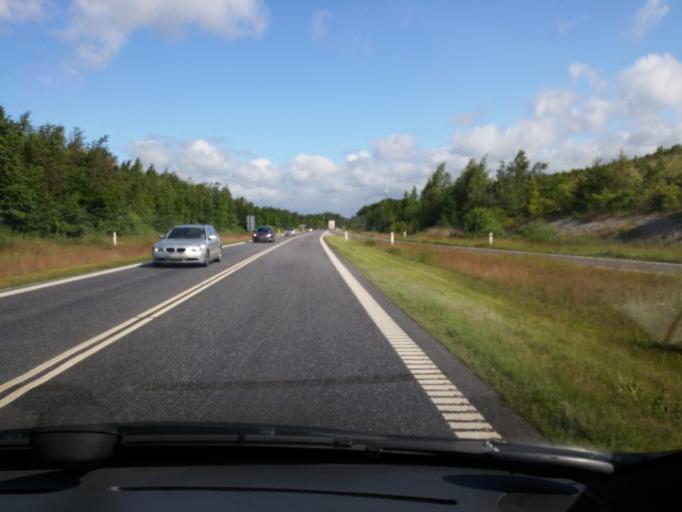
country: DK
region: Capital Region
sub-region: Hillerod Kommune
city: Hillerod
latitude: 55.9375
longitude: 12.2468
